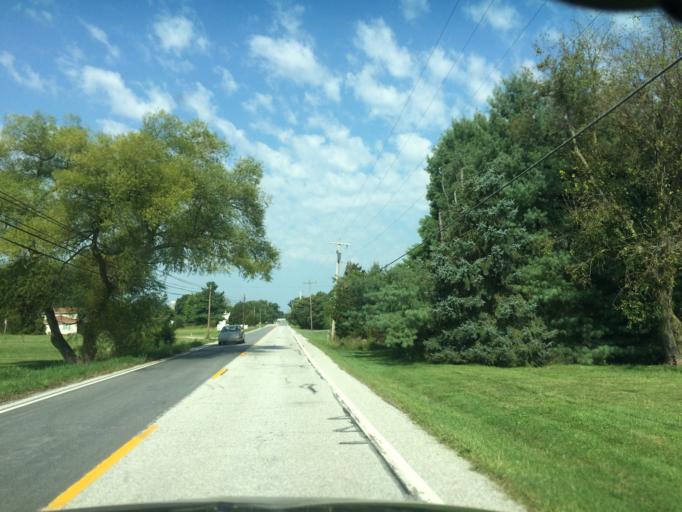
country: US
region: Maryland
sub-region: Carroll County
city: Taneytown
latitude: 39.6289
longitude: -77.1140
